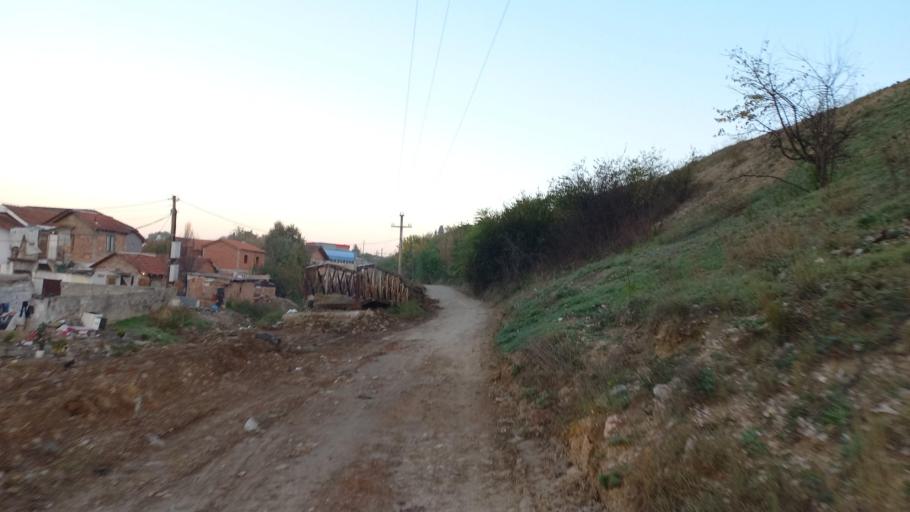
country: MK
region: Kumanovo
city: Kumanovo
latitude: 42.1410
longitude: 21.7246
